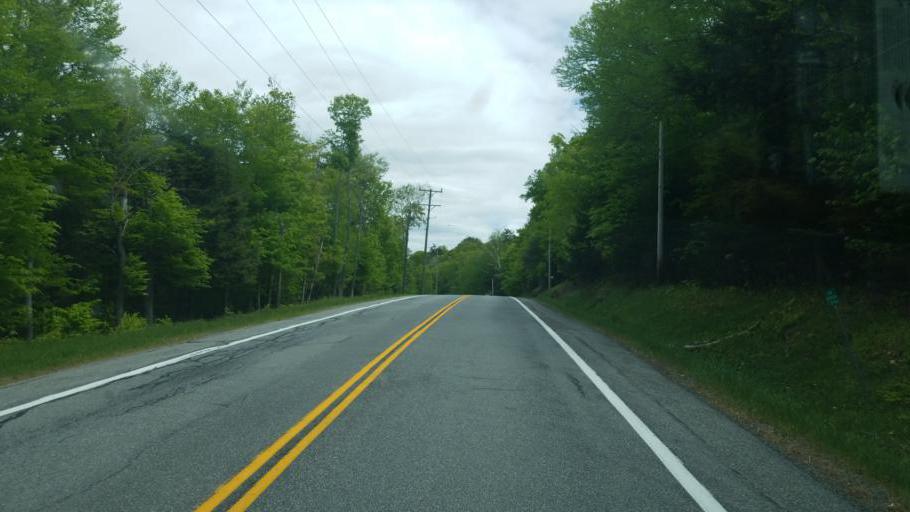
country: US
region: New York
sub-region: Franklin County
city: Tupper Lake
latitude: 43.8538
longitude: -74.4538
